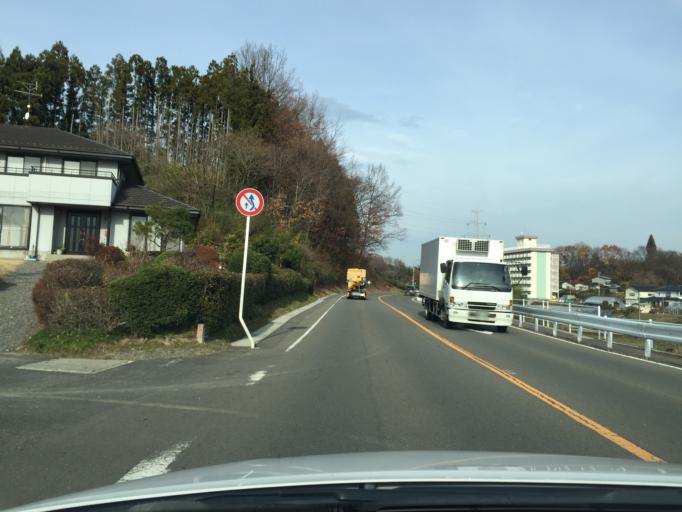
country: JP
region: Fukushima
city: Fukushima-shi
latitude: 37.6704
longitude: 140.4652
